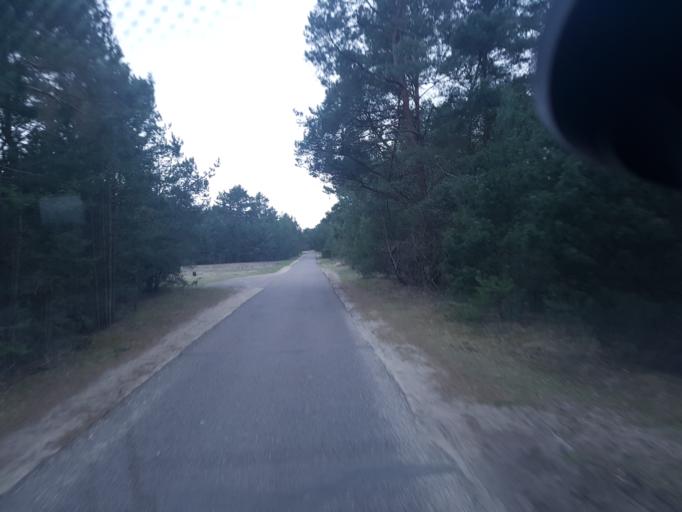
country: DE
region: Brandenburg
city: Eisenhuettenstadt
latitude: 52.1583
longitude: 14.6637
